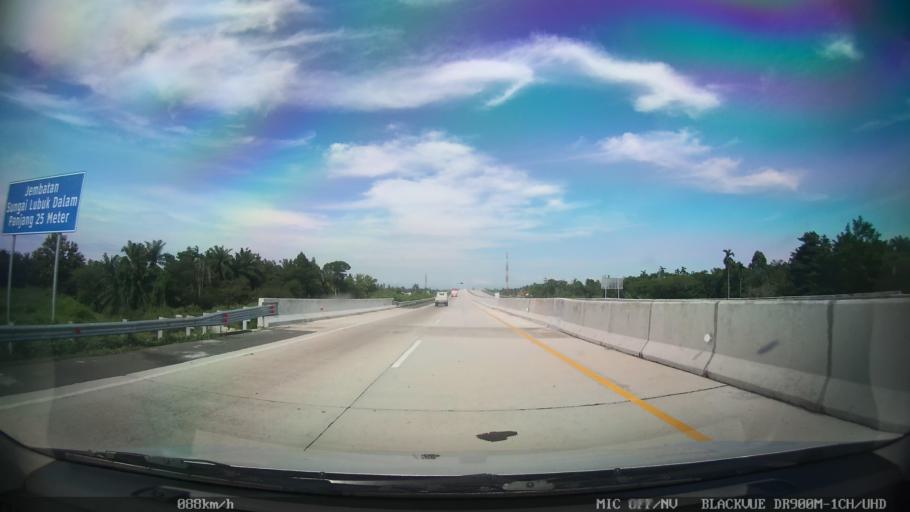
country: ID
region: North Sumatra
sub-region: Kabupaten Langkat
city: Stabat
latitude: 3.7134
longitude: 98.5088
